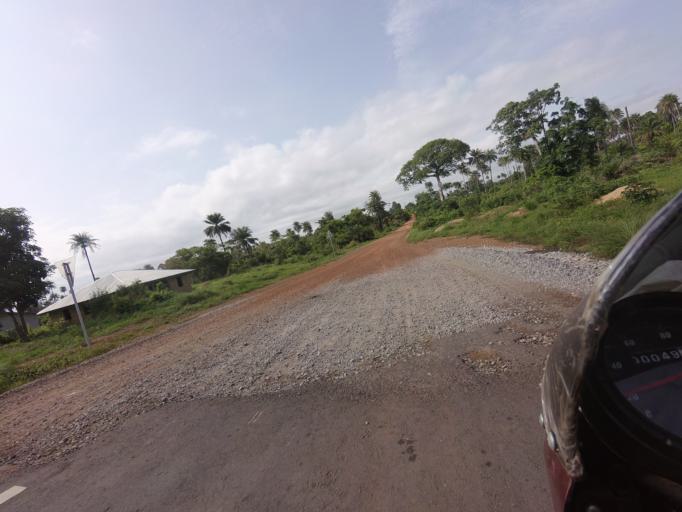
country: SL
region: Eastern Province
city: Mobai
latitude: 8.0023
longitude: -10.7569
